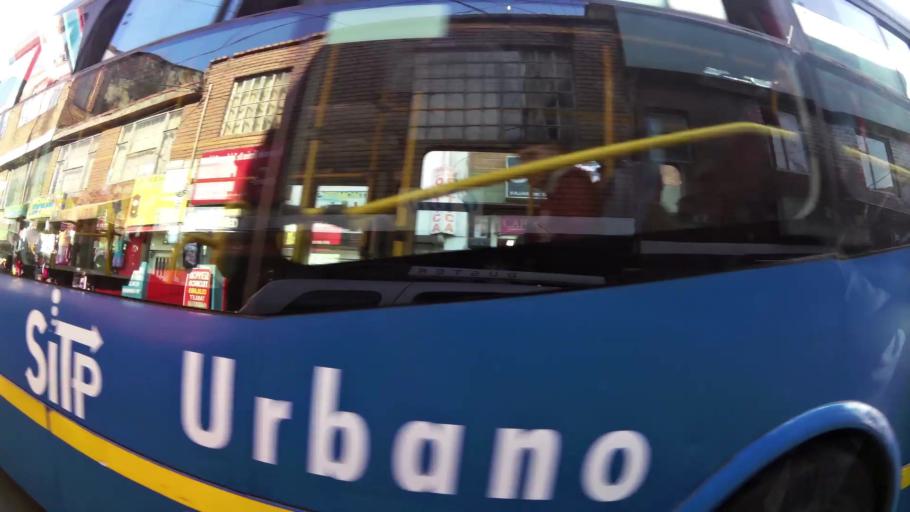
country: CO
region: Cundinamarca
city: Soacha
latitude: 4.5615
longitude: -74.1452
